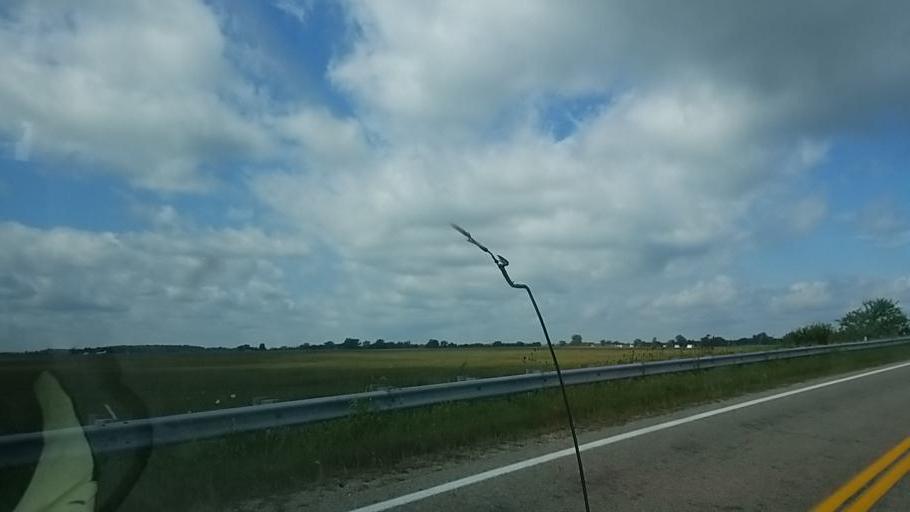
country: US
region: Ohio
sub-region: Madison County
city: Bethel
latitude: 39.7293
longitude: -83.3708
